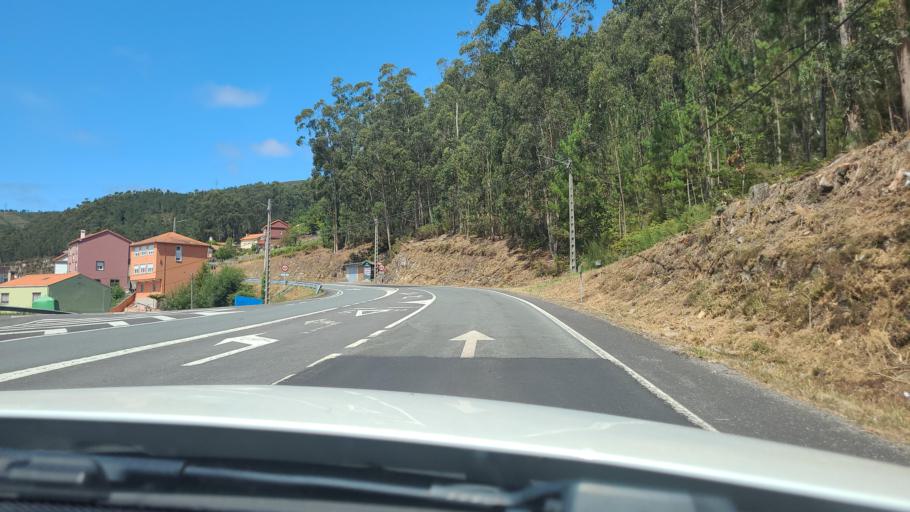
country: ES
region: Galicia
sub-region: Provincia da Coruna
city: Corcubion
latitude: 42.9147
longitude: -9.1455
